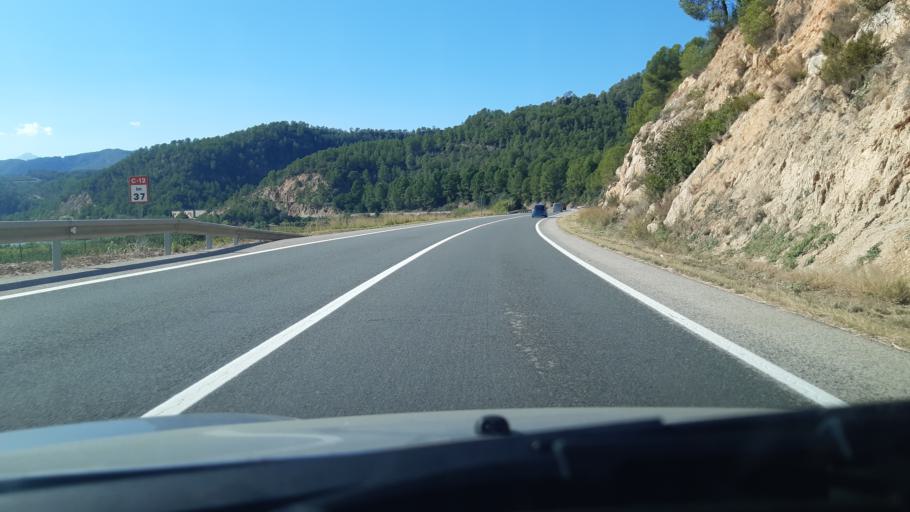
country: ES
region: Catalonia
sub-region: Provincia de Tarragona
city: Benifallet
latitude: 40.9586
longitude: 0.4937
